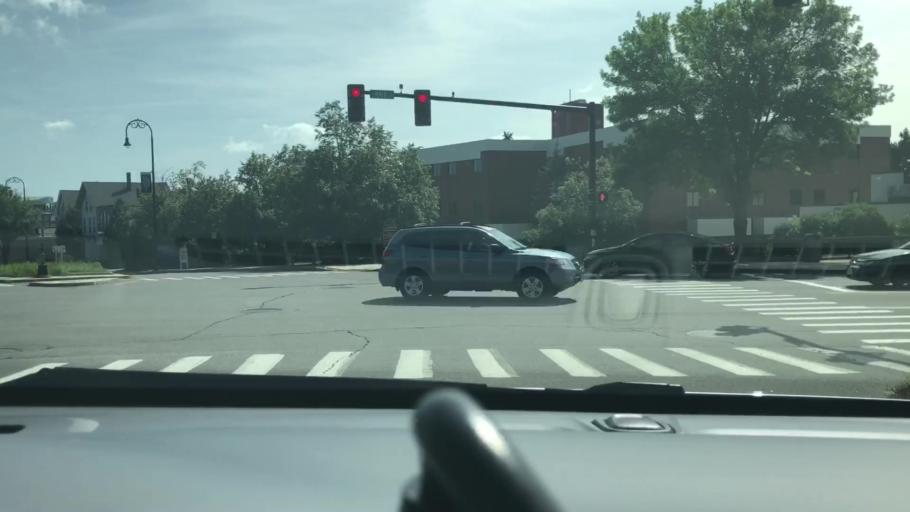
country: US
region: New Hampshire
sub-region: Hillsborough County
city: Manchester
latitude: 42.9837
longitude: -71.4742
